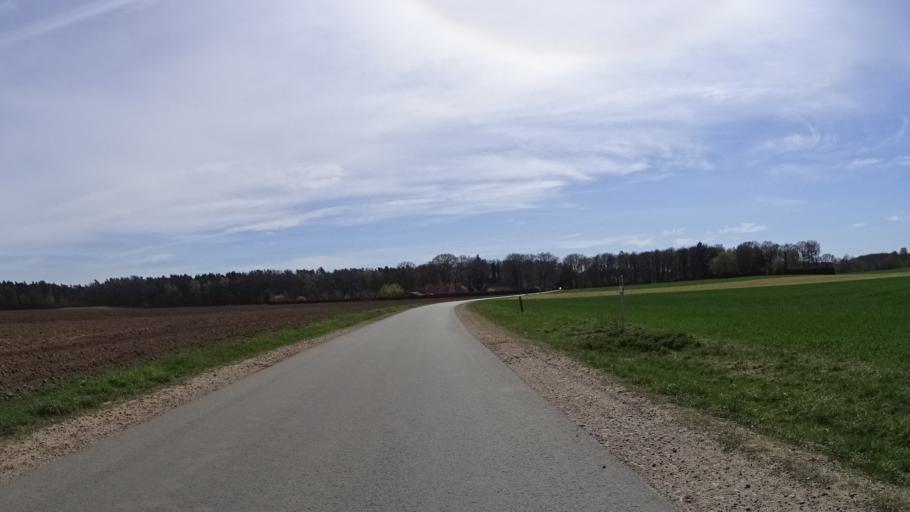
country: DE
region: Lower Saxony
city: Emsburen
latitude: 52.4444
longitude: 7.3429
